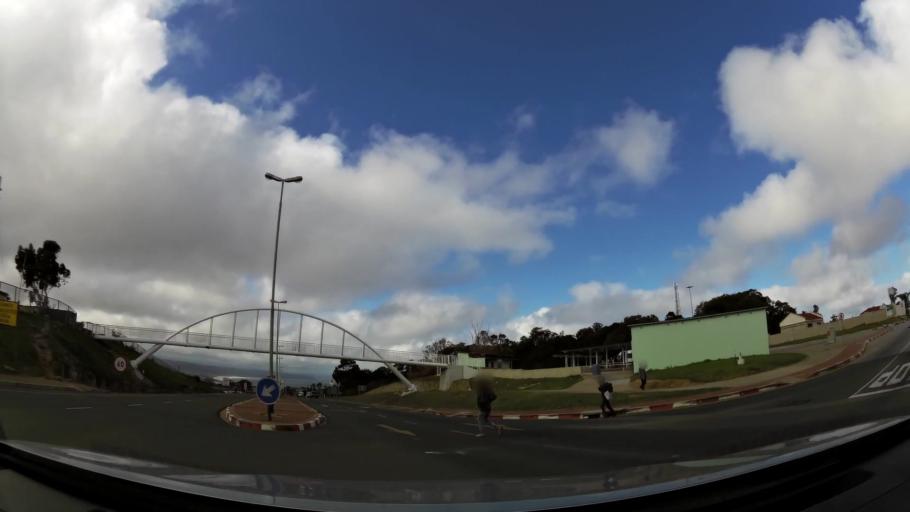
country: ZA
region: Western Cape
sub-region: Eden District Municipality
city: Plettenberg Bay
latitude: -34.0513
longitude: 23.3535
